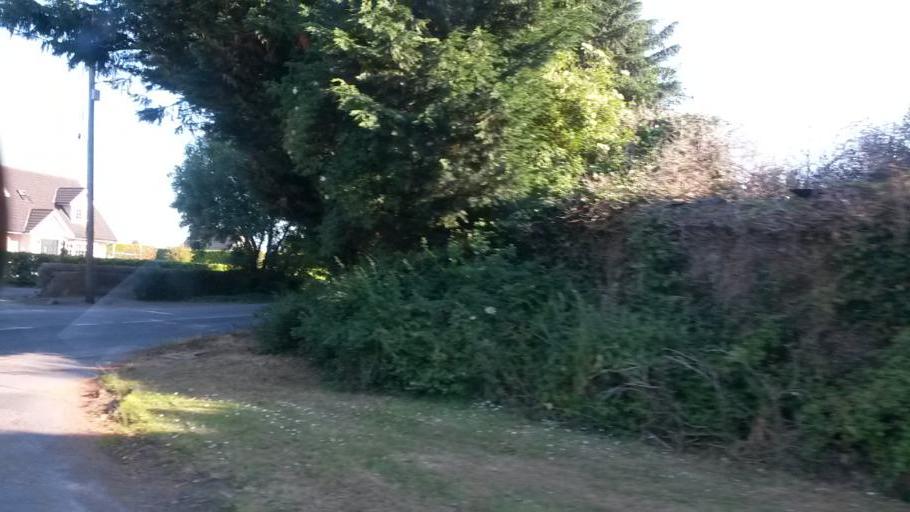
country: IE
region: Leinster
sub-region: An Mhi
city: Ashbourne
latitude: 53.4742
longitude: -6.3196
